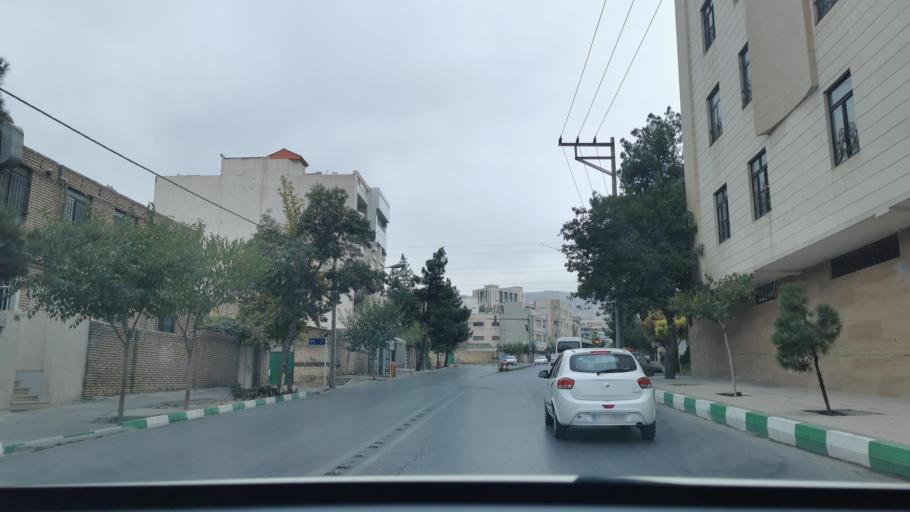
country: IR
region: Razavi Khorasan
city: Mashhad
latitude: 36.3065
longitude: 59.5010
